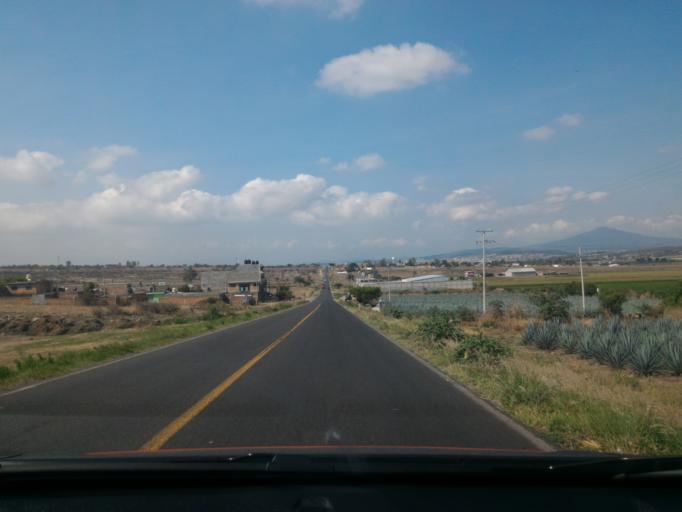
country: MX
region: Guanajuato
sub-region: Penjamo
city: Estacion la Piedad
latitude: 20.4217
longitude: -101.9935
